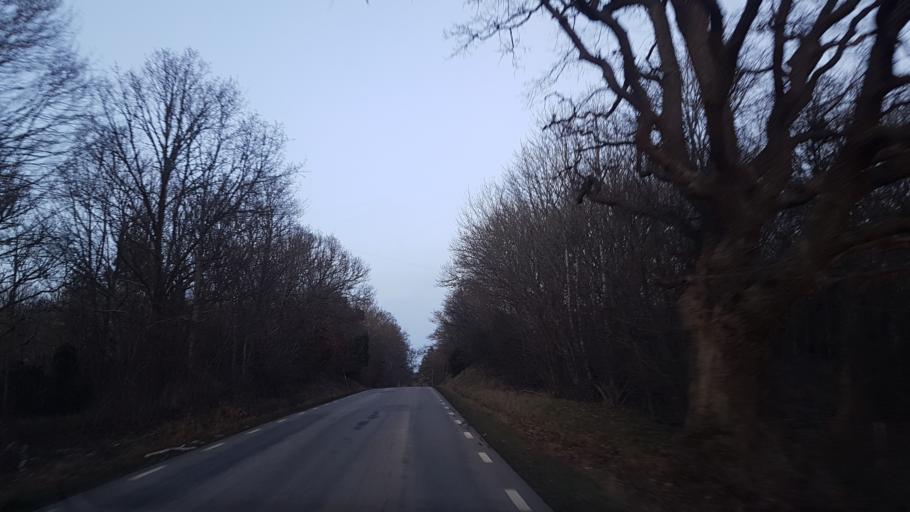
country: SE
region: Blekinge
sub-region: Karlskrona Kommun
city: Jaemjoe
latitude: 56.1199
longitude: 15.8276
